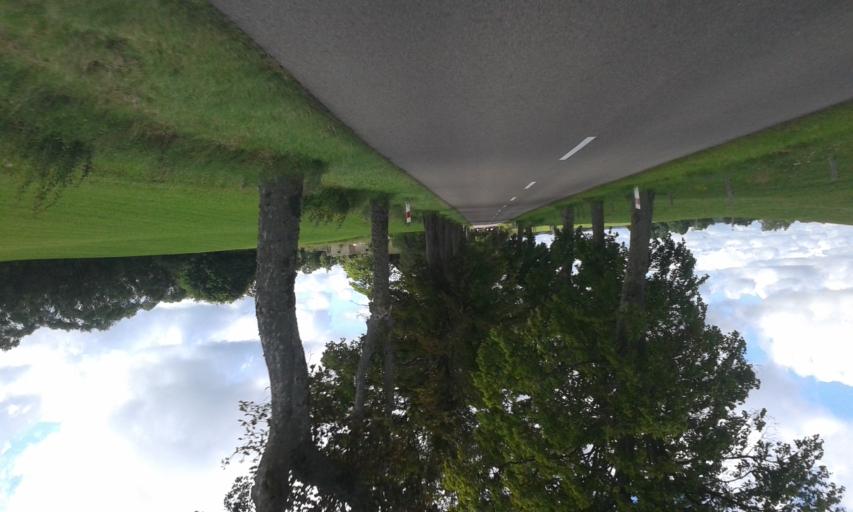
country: PL
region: West Pomeranian Voivodeship
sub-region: Powiat koszalinski
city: Bobolice
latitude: 53.9847
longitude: 16.6786
